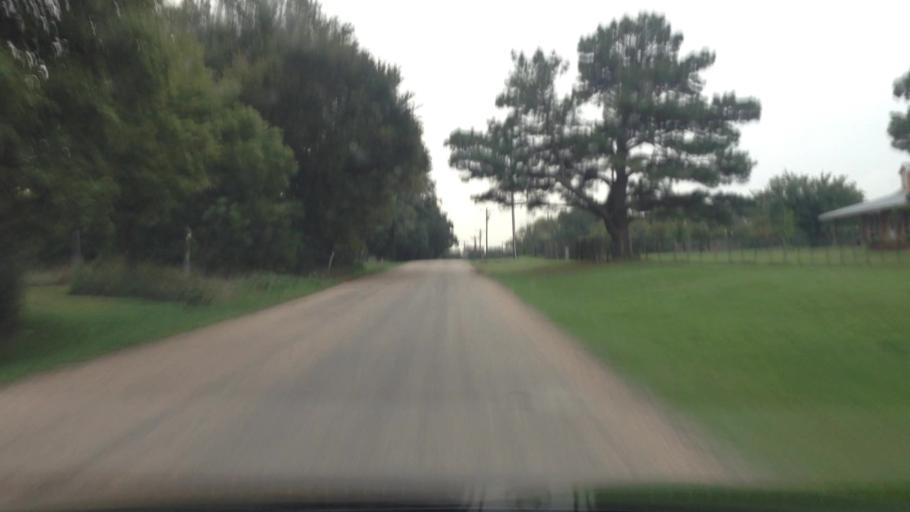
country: US
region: Texas
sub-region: Johnson County
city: Joshua
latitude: 32.4803
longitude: -97.3417
